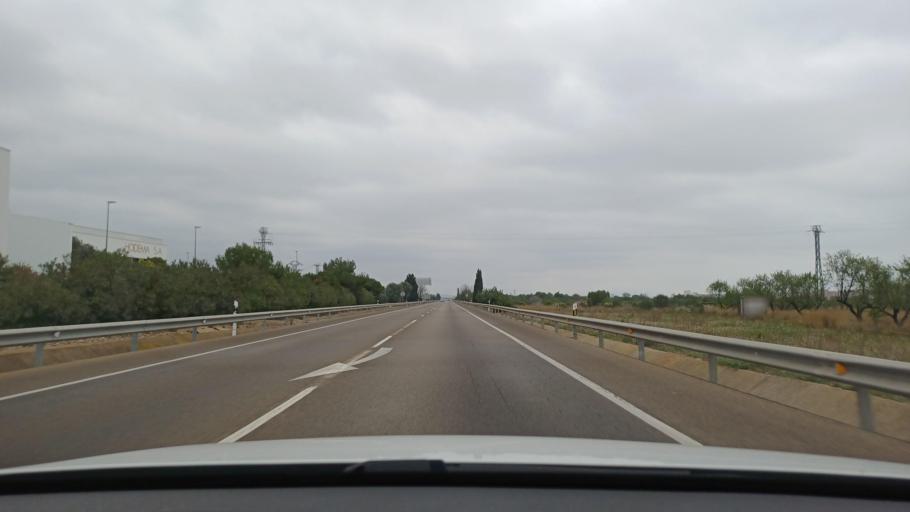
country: ES
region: Valencia
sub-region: Provincia de Castello
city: Orpesa/Oropesa del Mar
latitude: 40.1075
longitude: 0.1373
